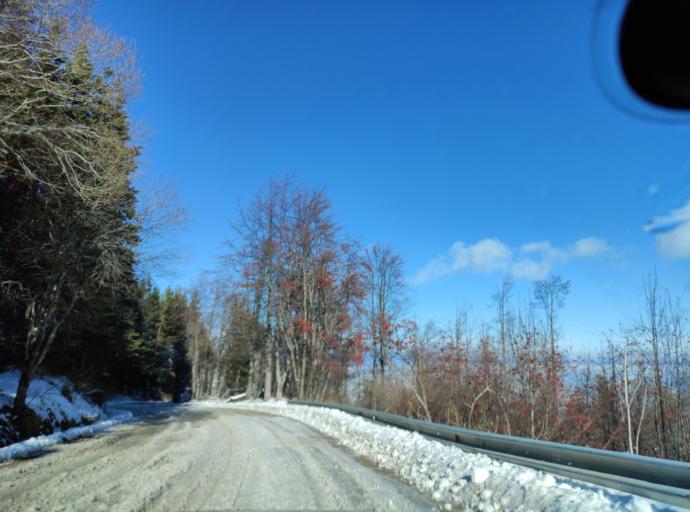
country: BG
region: Sofia-Capital
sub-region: Stolichna Obshtina
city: Sofia
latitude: 42.5894
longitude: 23.3119
